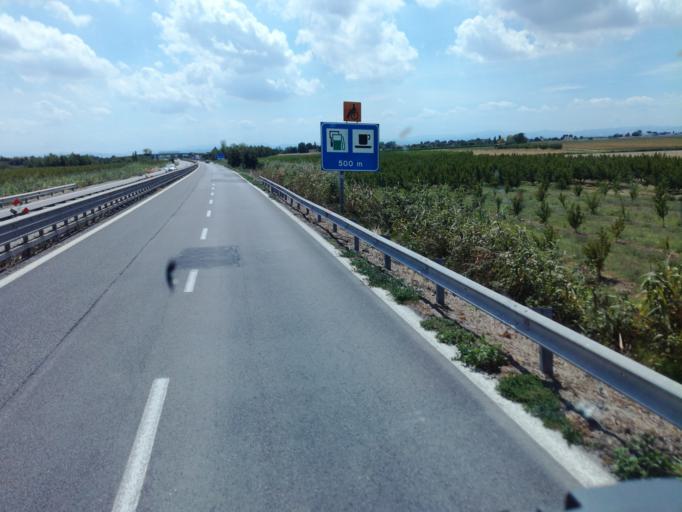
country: IT
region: Emilia-Romagna
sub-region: Provincia di Ravenna
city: Madonna Dell'Albero
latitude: 44.3688
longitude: 12.2030
